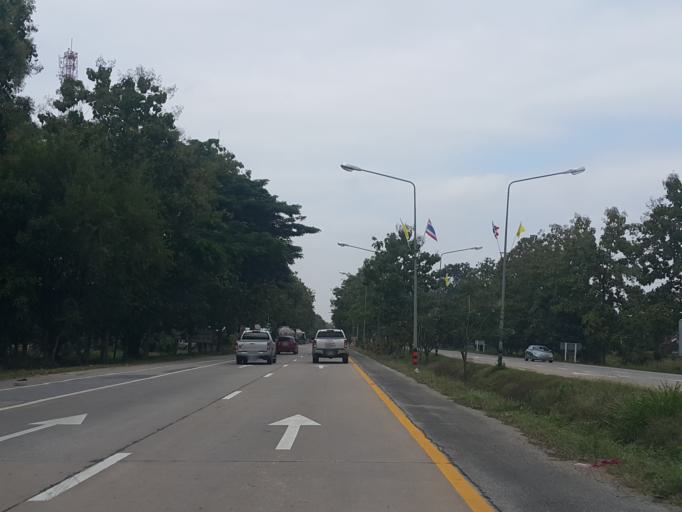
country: TH
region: Lamphun
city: Mae Tha
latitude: 18.5220
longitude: 99.0867
